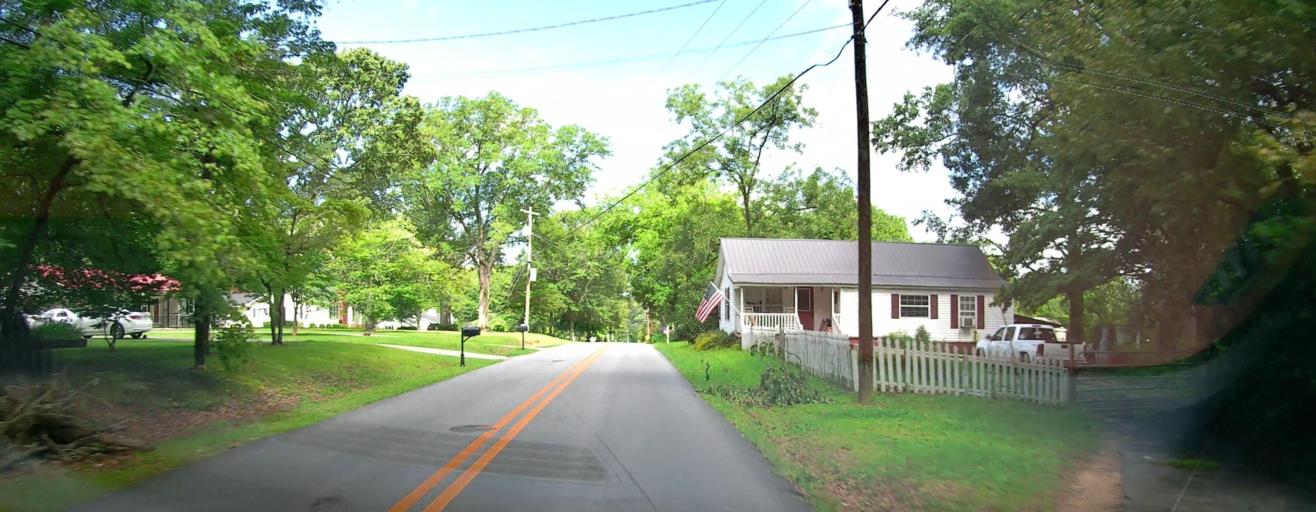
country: US
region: Georgia
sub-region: Peach County
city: Byron
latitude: 32.6555
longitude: -83.7634
